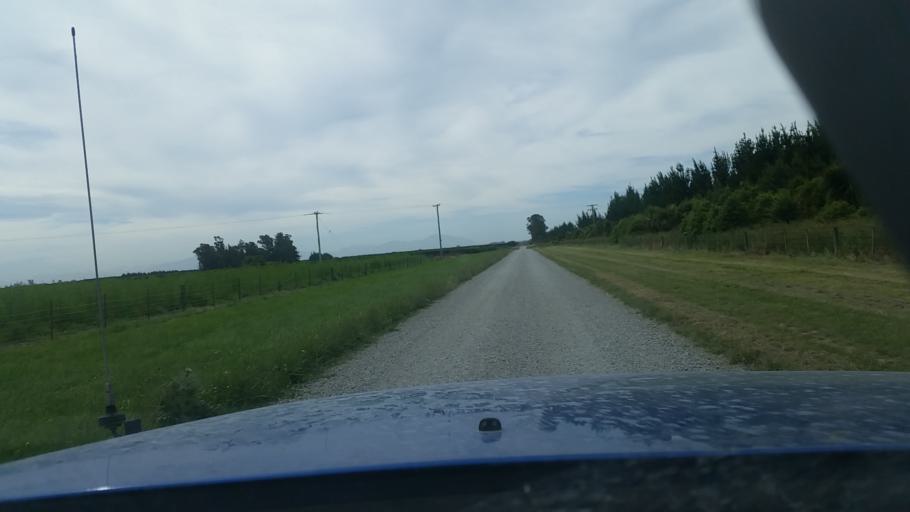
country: NZ
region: Canterbury
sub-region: Ashburton District
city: Tinwald
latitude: -44.0286
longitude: 171.7820
